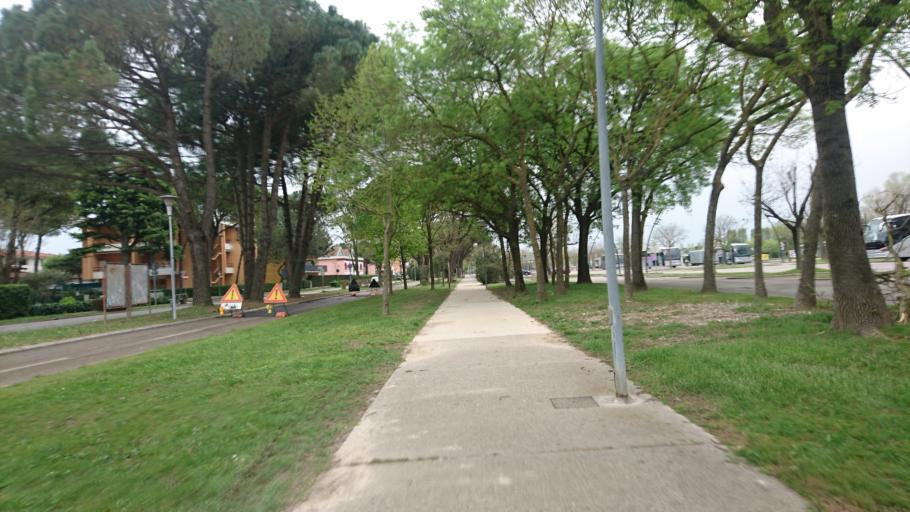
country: IT
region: Veneto
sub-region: Provincia di Venezia
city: Bibione
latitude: 45.6384
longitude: 13.0539
